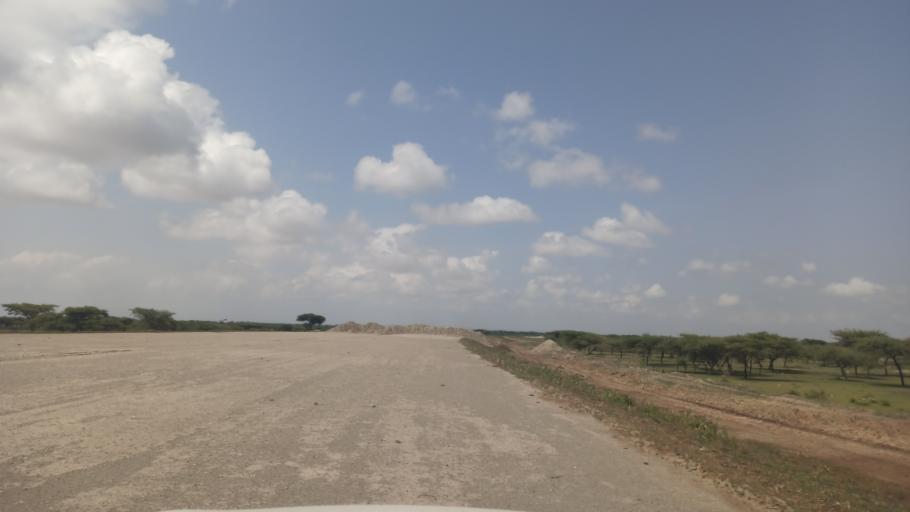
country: ET
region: Oromiya
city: Ziway
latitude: 7.6646
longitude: 38.6836
